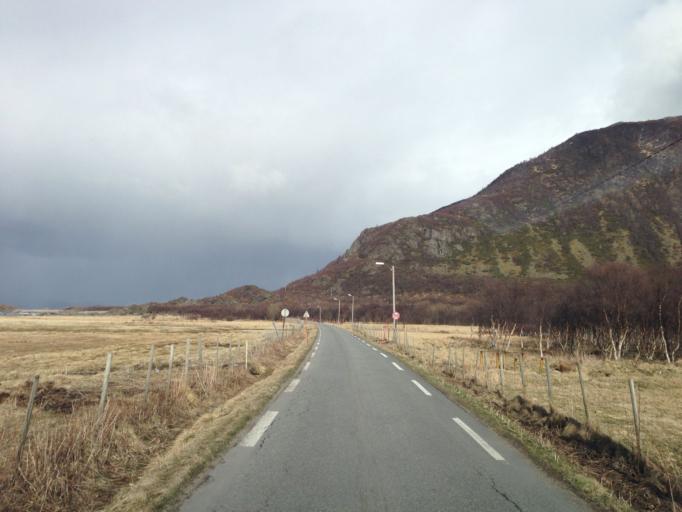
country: NO
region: Nordland
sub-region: Vagan
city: Svolvaer
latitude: 68.3959
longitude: 14.4879
